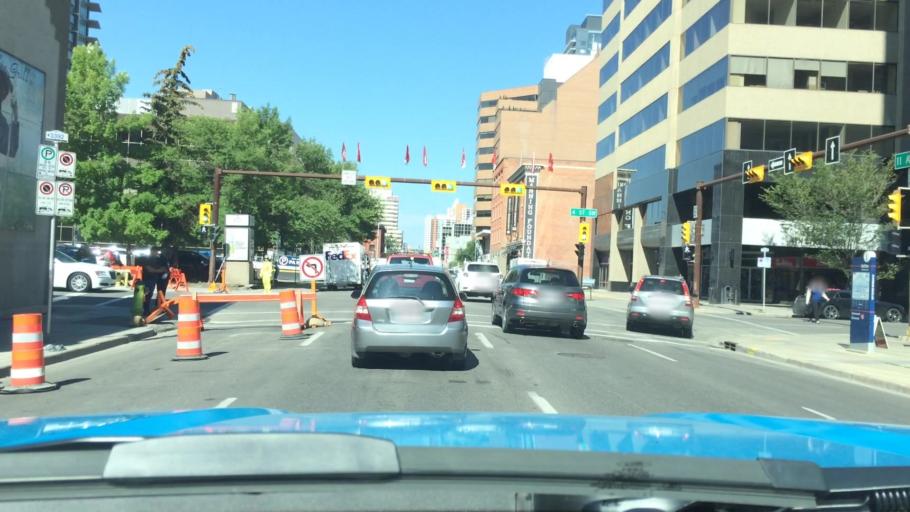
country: CA
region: Alberta
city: Calgary
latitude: 51.0426
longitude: -114.0712
